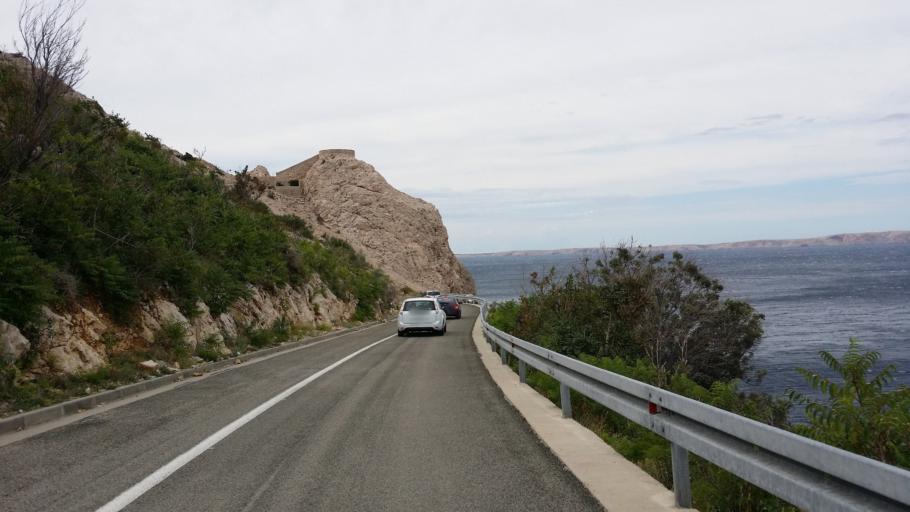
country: HR
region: Primorsko-Goranska
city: Banjol
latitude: 44.7030
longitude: 14.8959
